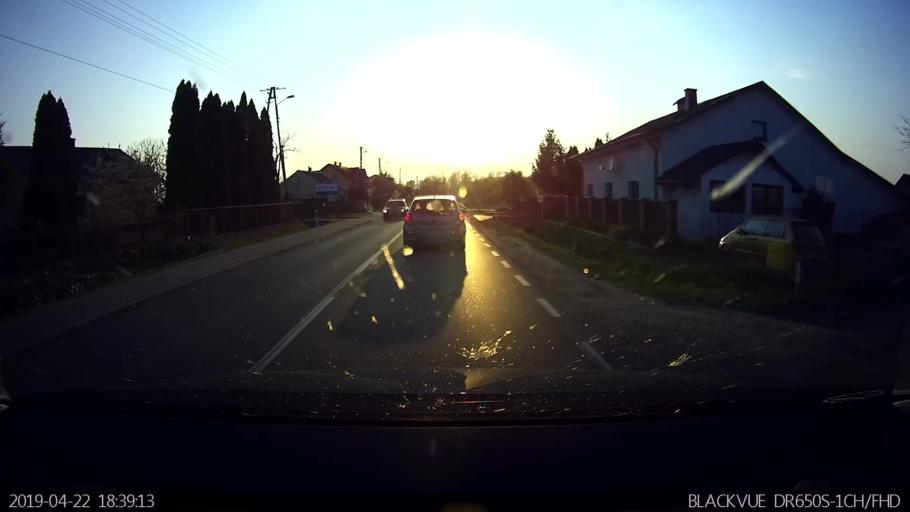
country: PL
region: Masovian Voivodeship
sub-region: Powiat wolominski
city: Dabrowka
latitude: 52.4416
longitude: 21.2885
